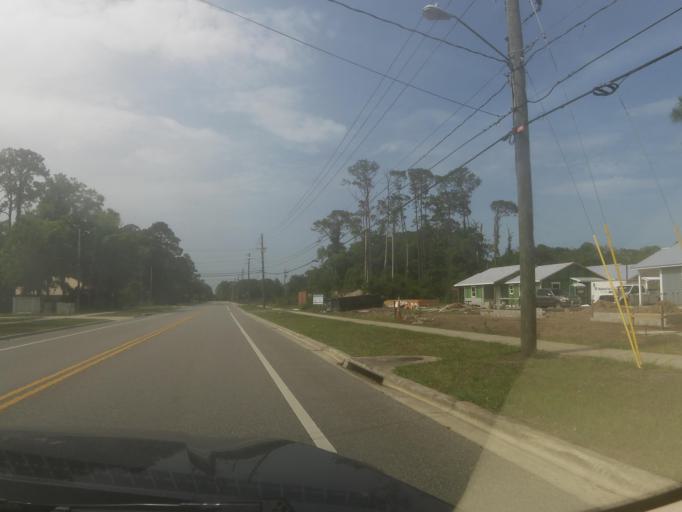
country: US
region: Florida
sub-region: Saint Johns County
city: Saint Augustine
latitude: 29.8929
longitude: -81.3448
